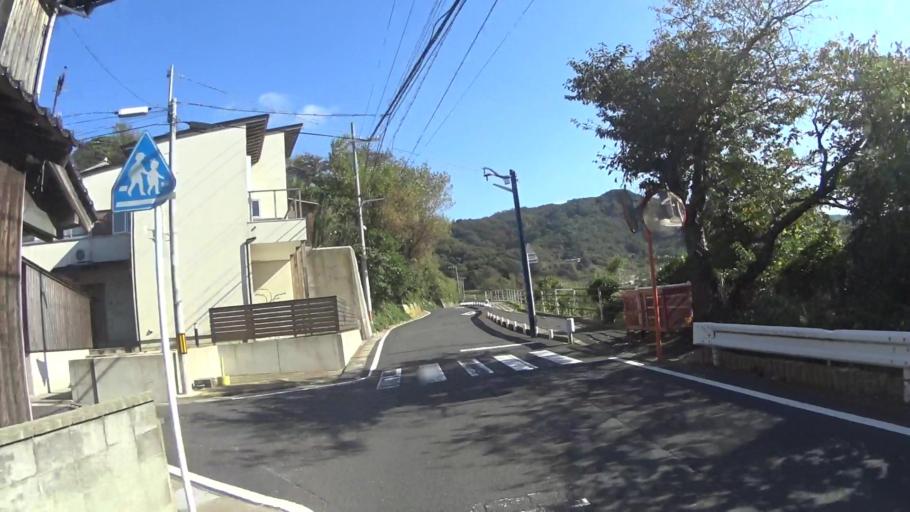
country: JP
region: Kyoto
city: Miyazu
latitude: 35.7344
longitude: 135.0856
